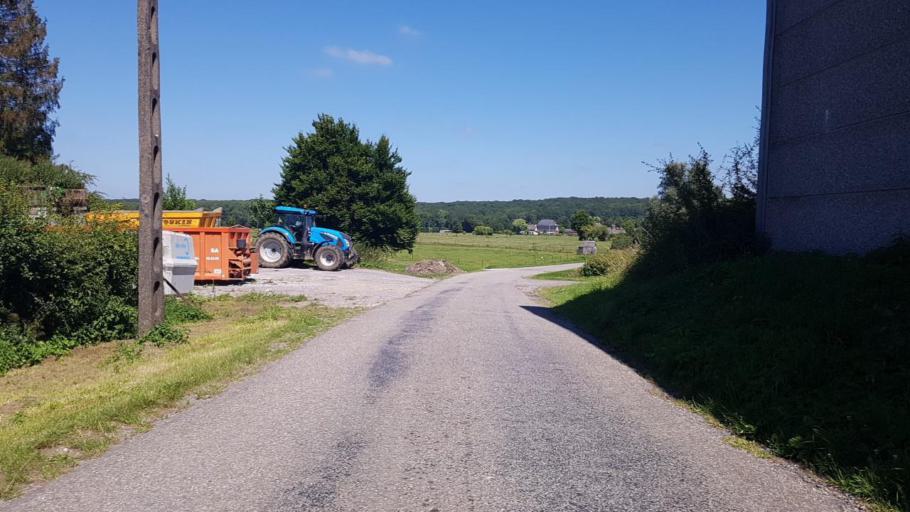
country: BE
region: Wallonia
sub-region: Province du Hainaut
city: Momignies
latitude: 50.0686
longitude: 4.2355
